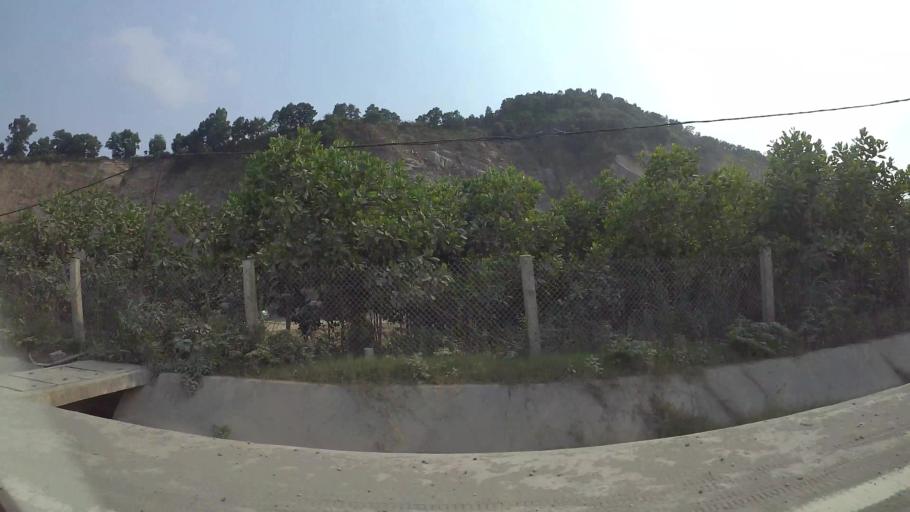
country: VN
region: Da Nang
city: Lien Chieu
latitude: 16.0417
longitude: 108.1653
